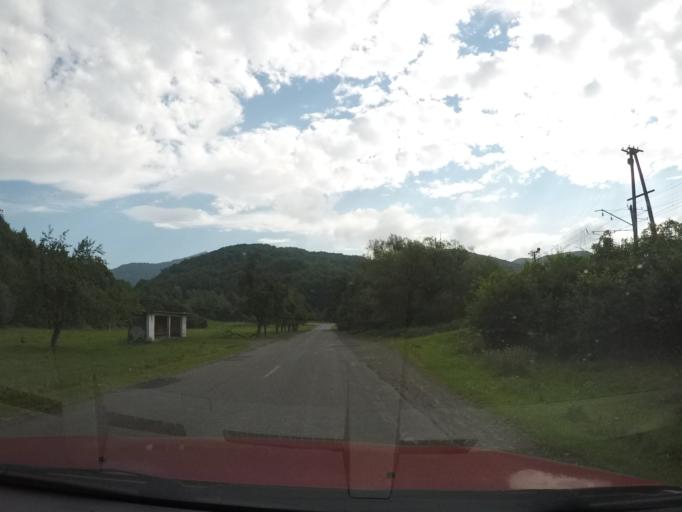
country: UA
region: Zakarpattia
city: Velykyi Bereznyi
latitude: 48.9520
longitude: 22.5446
